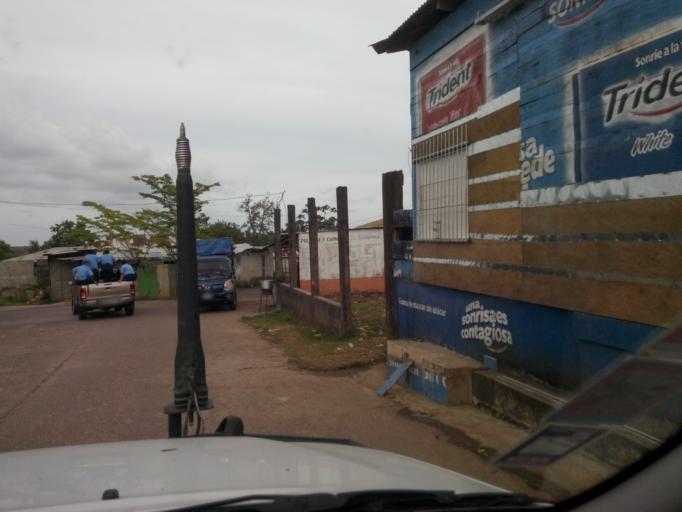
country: NI
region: Atlantico Sur
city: Bluefields
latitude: 12.0288
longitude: -83.7698
